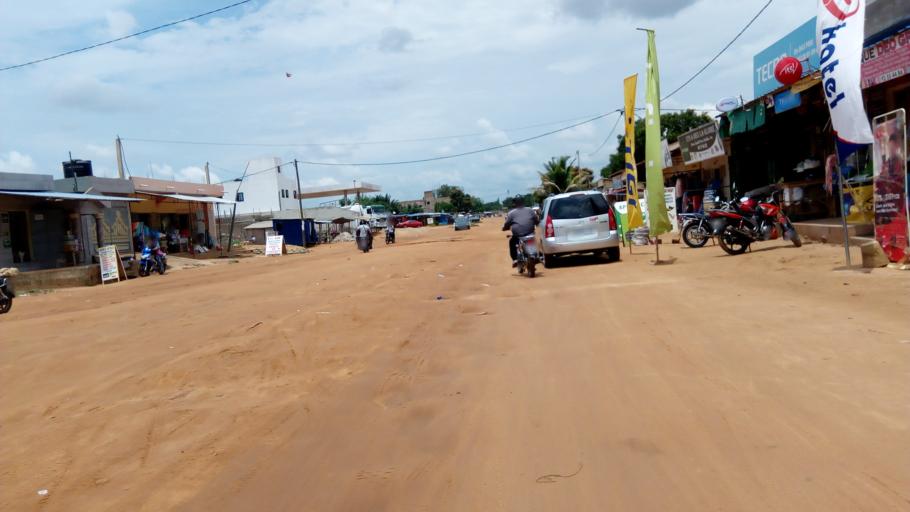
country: TG
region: Maritime
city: Lome
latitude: 6.2283
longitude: 1.1578
